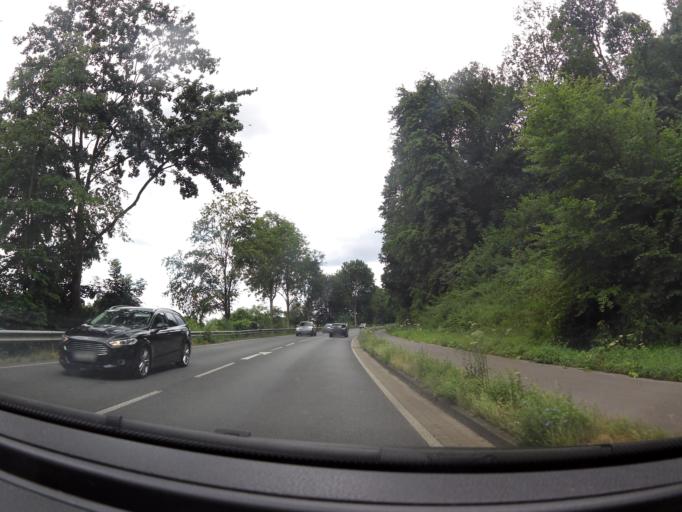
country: DE
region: North Rhine-Westphalia
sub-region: Regierungsbezirk Dusseldorf
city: Xanten
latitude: 51.6507
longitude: 6.4746
